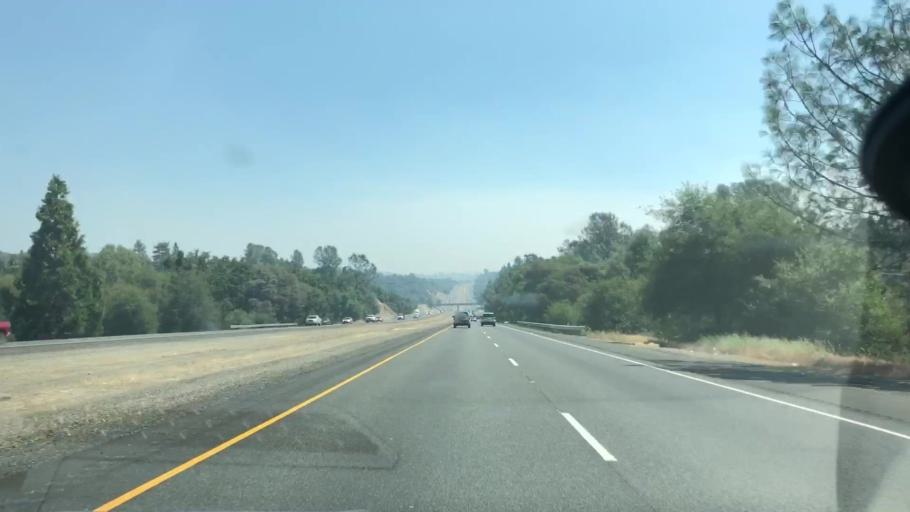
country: US
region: California
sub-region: El Dorado County
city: Deer Park
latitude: 38.7010
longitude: -120.8671
